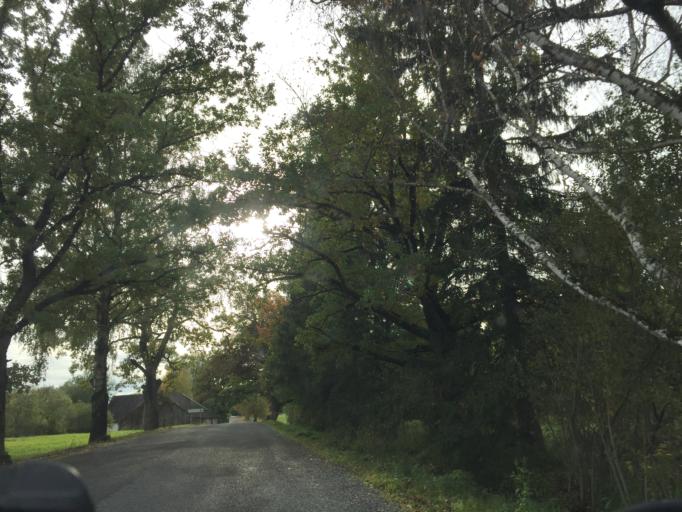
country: LV
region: Auces Novads
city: Auce
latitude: 56.5435
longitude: 23.0016
